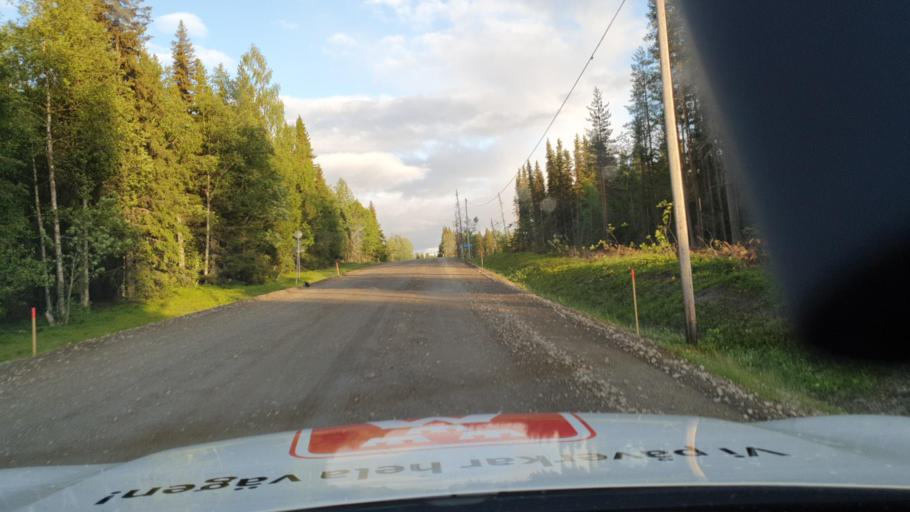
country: SE
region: Vaesterbotten
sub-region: Lycksele Kommun
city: Soderfors
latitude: 64.6526
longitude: 17.8479
